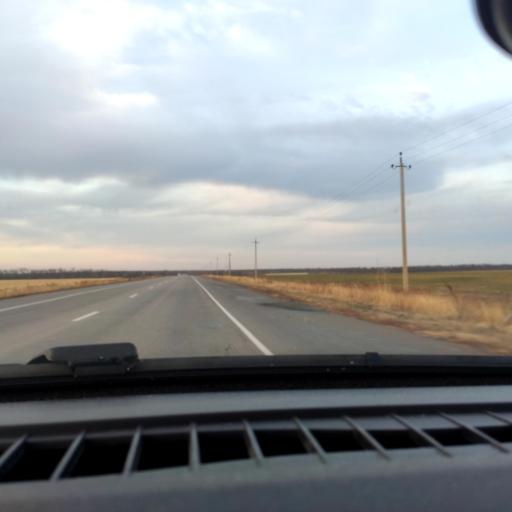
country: RU
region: Voronezj
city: Devitsa
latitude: 51.5629
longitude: 38.9738
